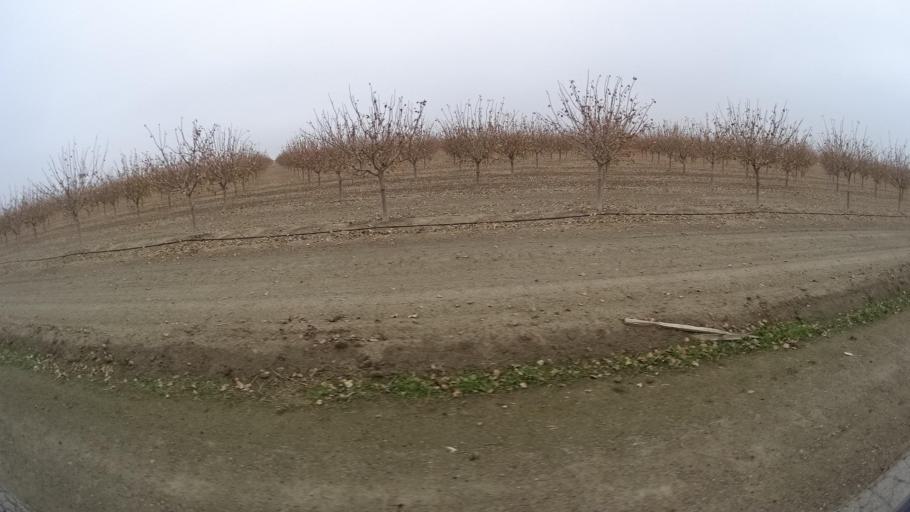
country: US
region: California
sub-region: Kern County
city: Wasco
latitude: 35.6859
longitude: -119.5086
